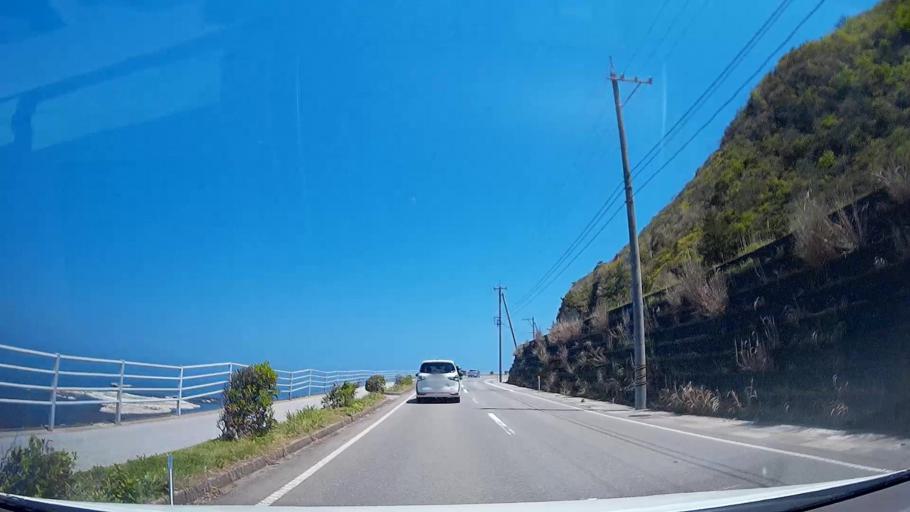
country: JP
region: Ishikawa
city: Nanao
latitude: 37.4789
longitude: 137.1007
